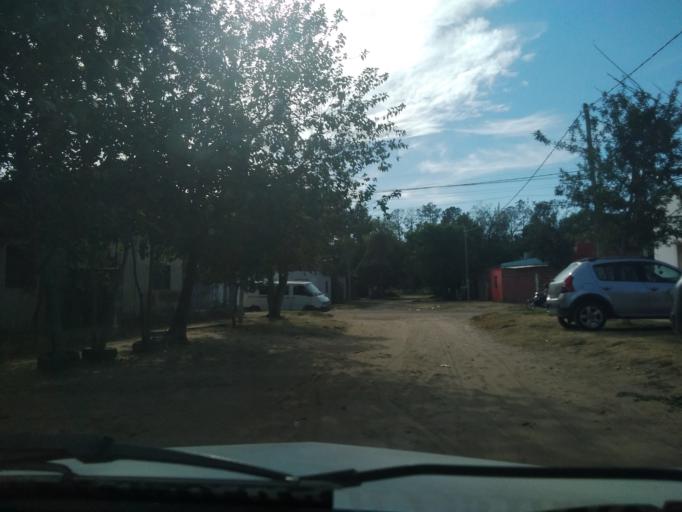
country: AR
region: Corrientes
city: Corrientes
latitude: -27.5077
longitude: -58.8055
